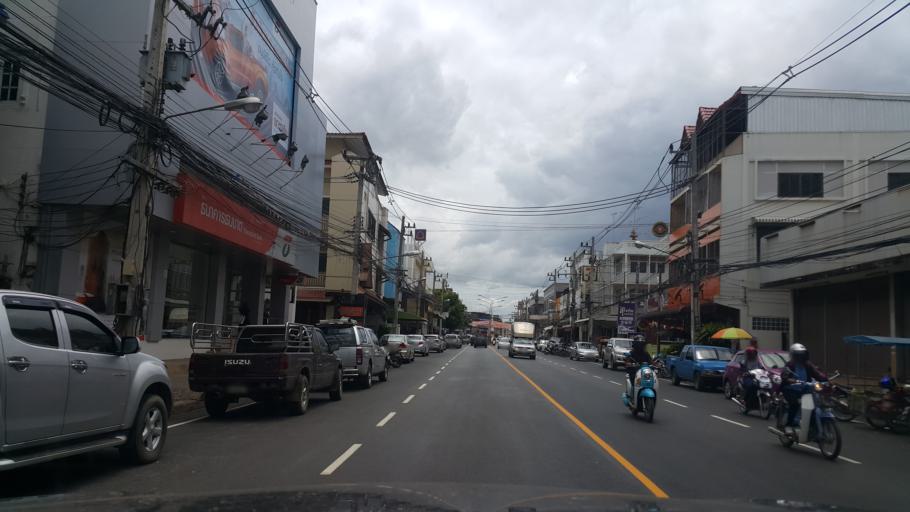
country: TH
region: Sukhothai
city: Sukhothai
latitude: 17.0086
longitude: 99.8223
